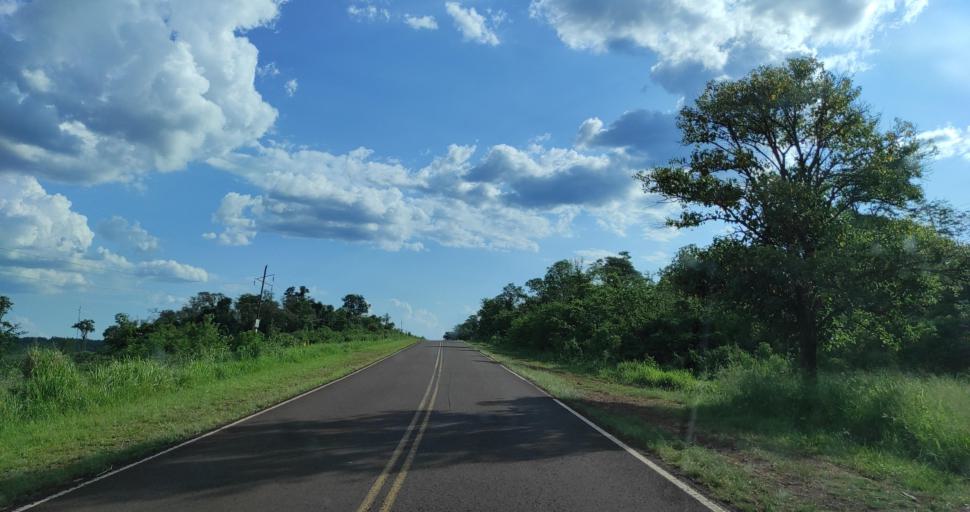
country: AR
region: Misiones
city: San Vicente
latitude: -26.3515
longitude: -54.2097
